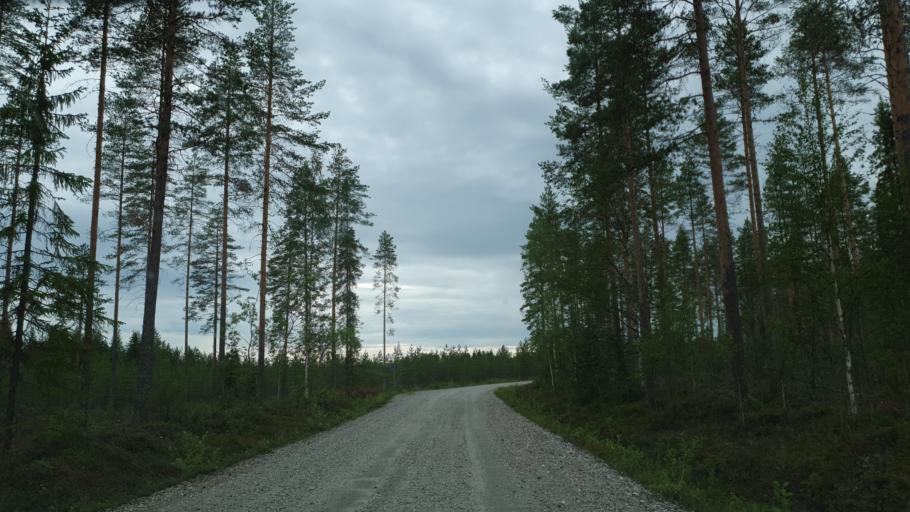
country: FI
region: Kainuu
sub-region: Kehys-Kainuu
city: Kuhmo
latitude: 64.4373
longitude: 29.5659
